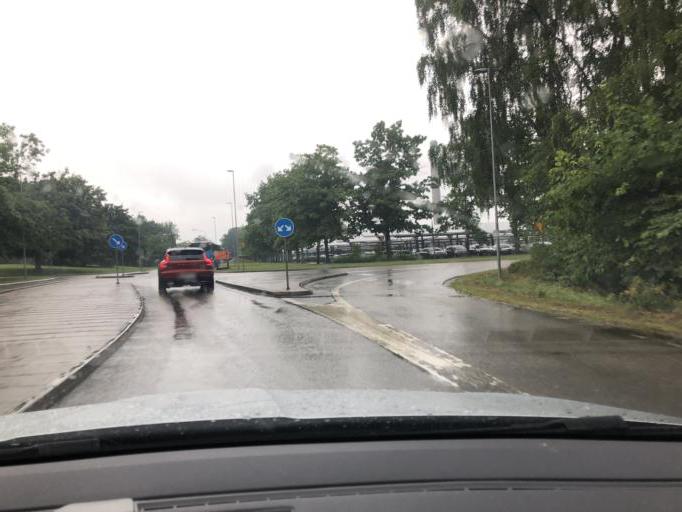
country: SE
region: Vaestra Goetaland
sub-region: Skovde Kommun
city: Skoevde
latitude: 58.4251
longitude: 13.8547
